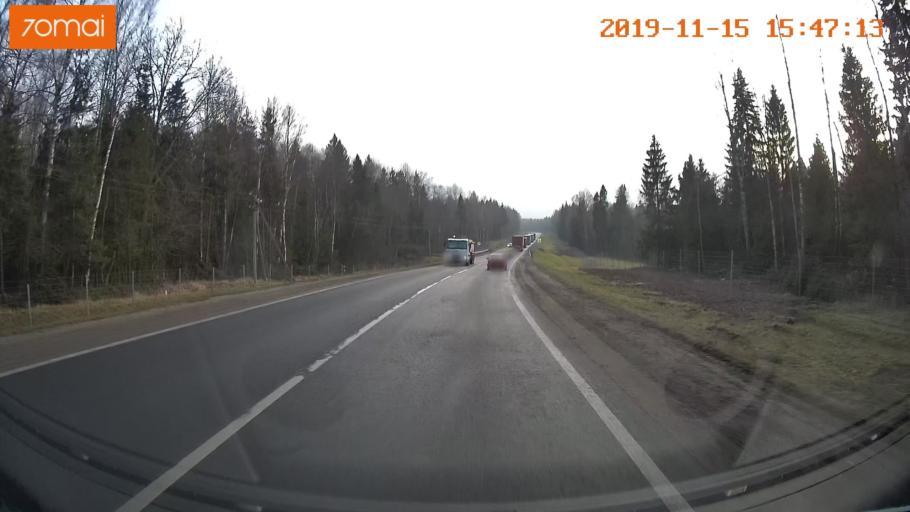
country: RU
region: Jaroslavl
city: Danilov
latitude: 57.9406
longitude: 40.0113
